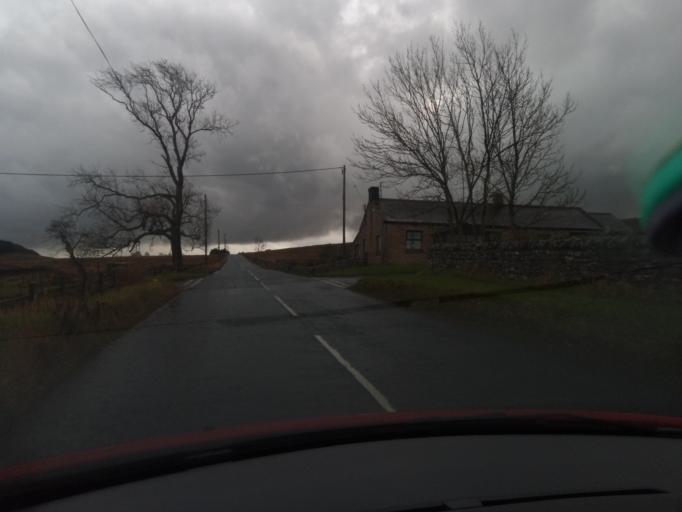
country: GB
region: England
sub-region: Northumberland
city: Birtley
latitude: 55.1325
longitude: -2.2480
